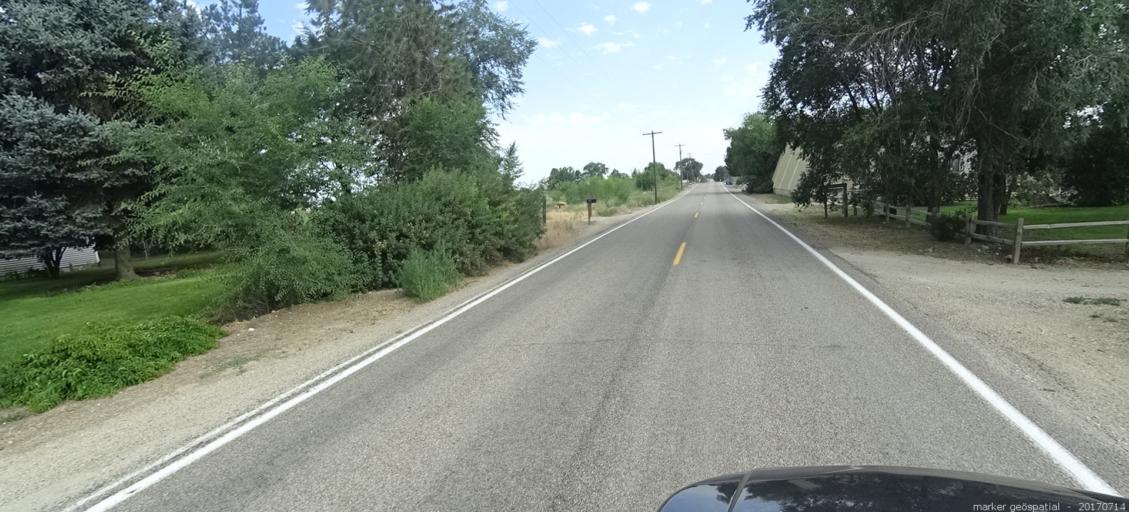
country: US
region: Idaho
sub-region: Ada County
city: Kuna
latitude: 43.4708
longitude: -116.3545
